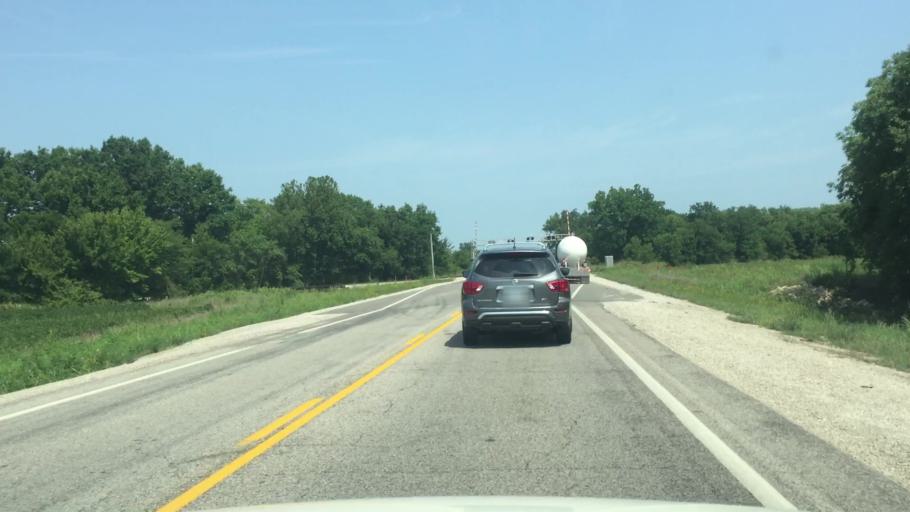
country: US
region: Kansas
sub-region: Montgomery County
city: Cherryvale
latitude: 37.1828
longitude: -95.5781
